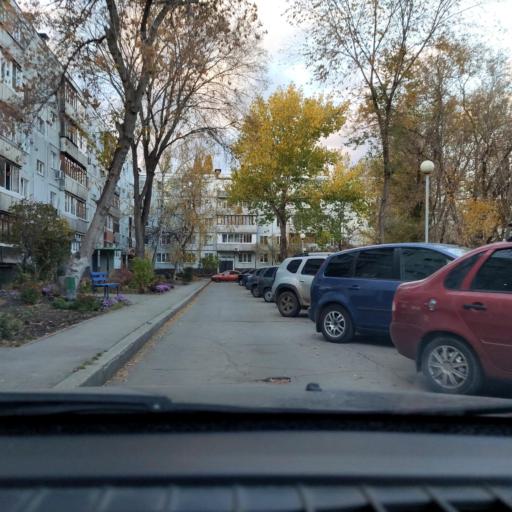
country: RU
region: Samara
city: Tol'yatti
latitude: 53.5257
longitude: 49.2705
